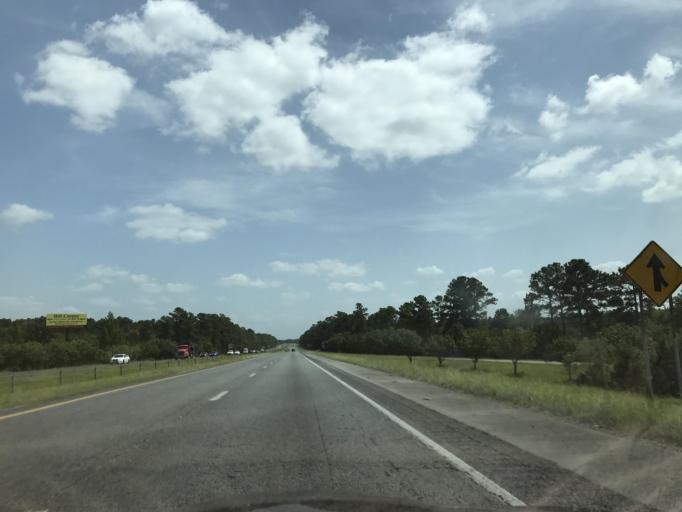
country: US
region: North Carolina
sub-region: Duplin County
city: Wallace
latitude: 34.7686
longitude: -77.9643
